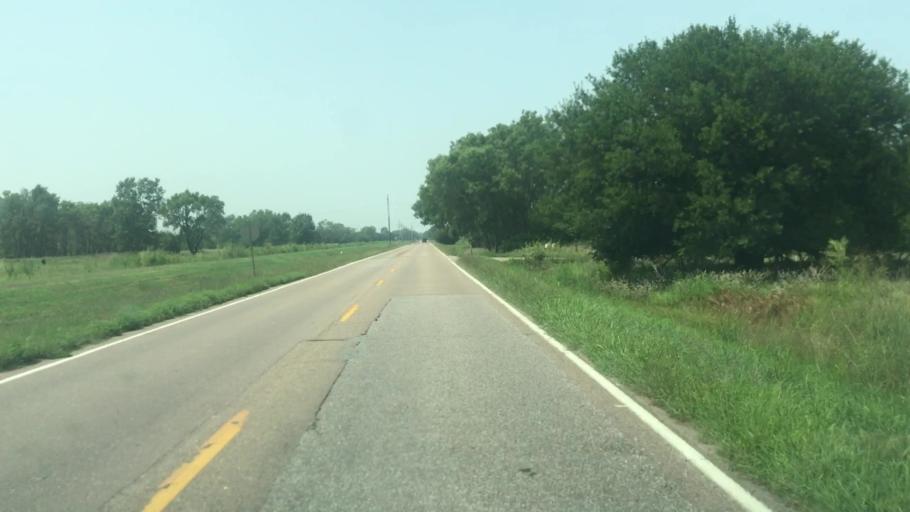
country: US
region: Nebraska
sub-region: Hall County
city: Grand Island
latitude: 40.9163
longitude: -98.3101
